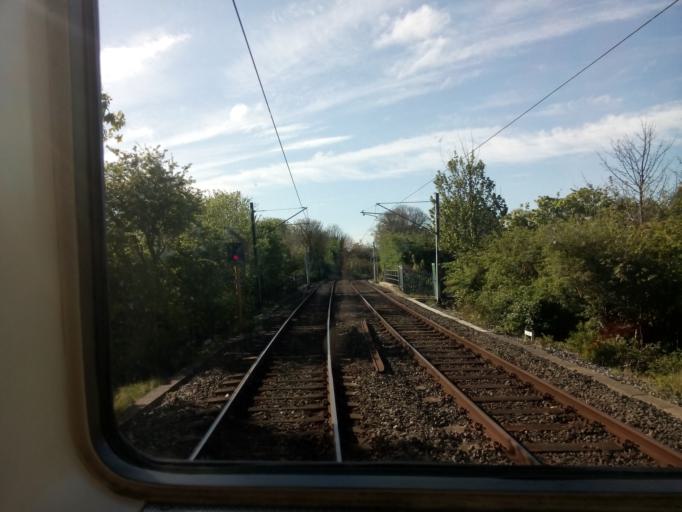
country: GB
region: England
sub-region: Newcastle upon Tyne
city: Gosforth
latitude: 55.0092
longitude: -1.6083
